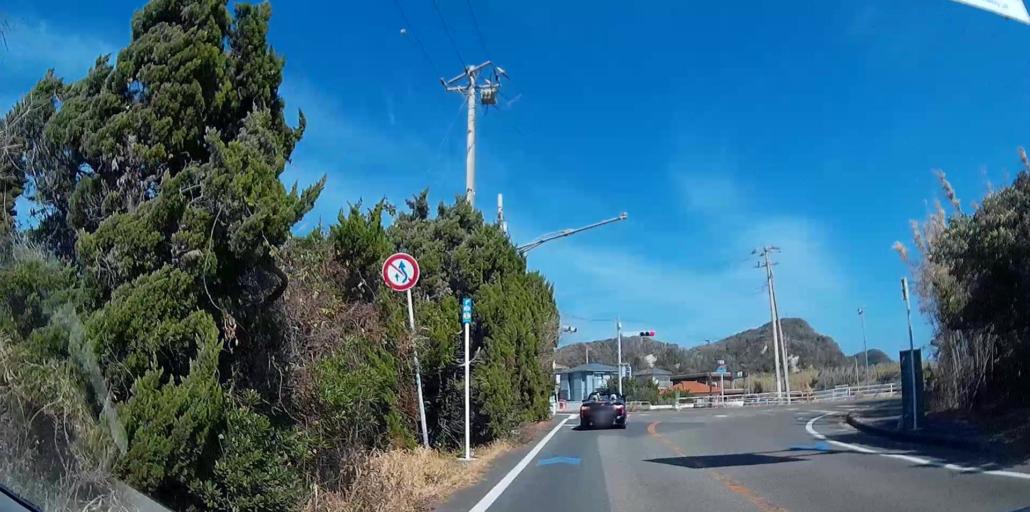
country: JP
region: Chiba
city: Tateyama
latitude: 34.9079
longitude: 139.8683
